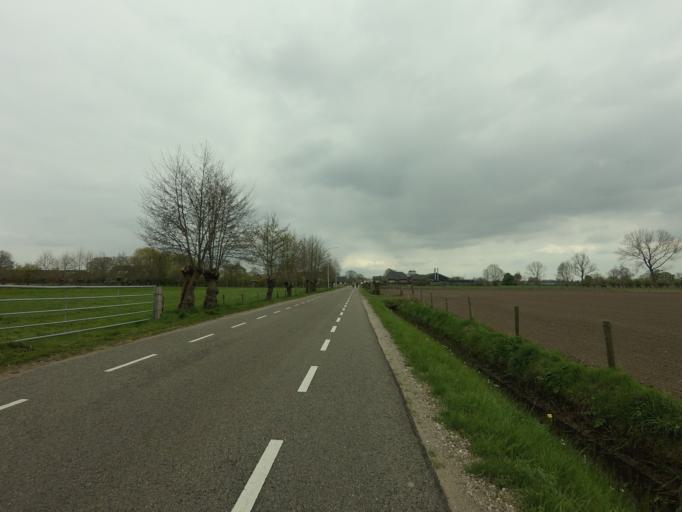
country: NL
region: Gelderland
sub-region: Gemeente Ede
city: Ederveen
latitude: 52.0679
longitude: 5.5686
